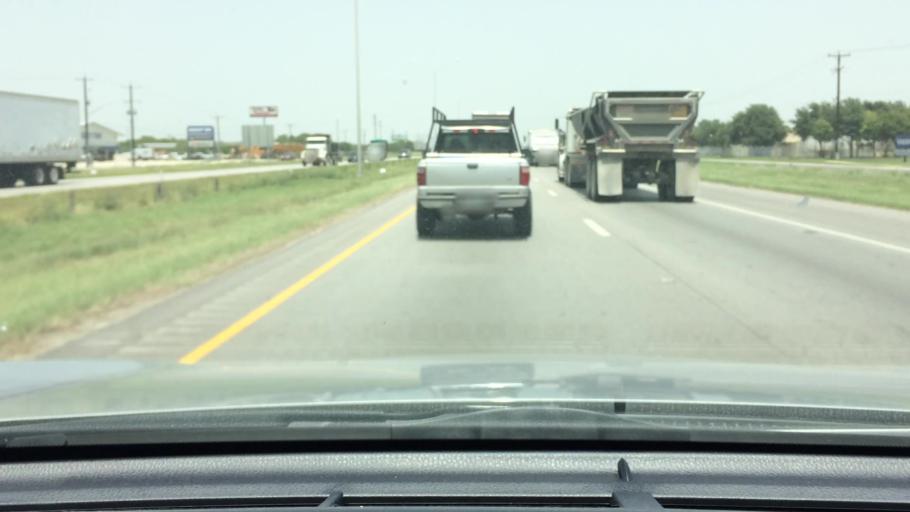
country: US
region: Texas
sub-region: Bexar County
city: China Grove
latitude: 29.4122
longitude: -98.3891
